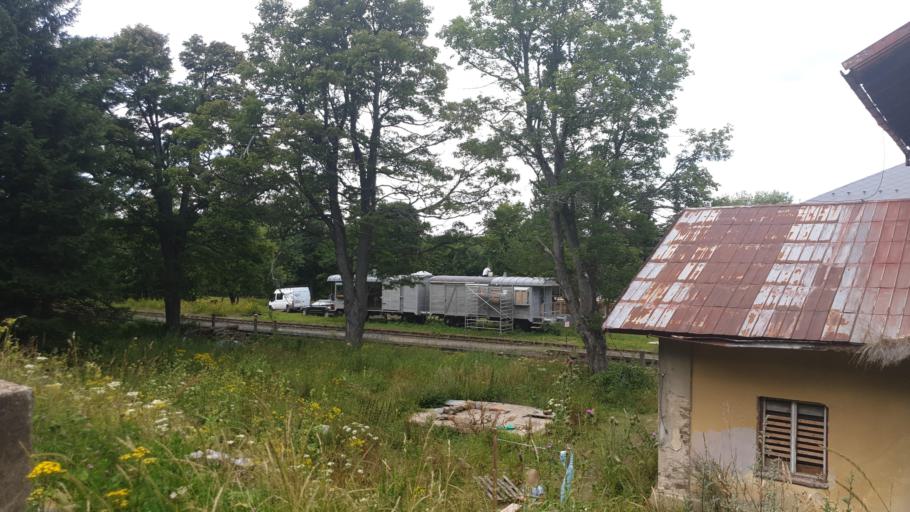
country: CZ
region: Ustecky
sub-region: Okres Chomutov
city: Kovarska
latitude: 50.4297
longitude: 13.0351
